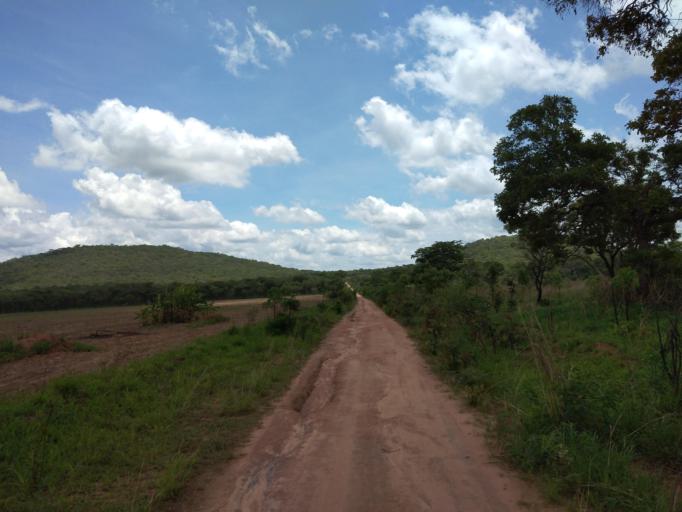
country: ZM
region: Central
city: Mkushi
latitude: -13.9129
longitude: 29.8665
